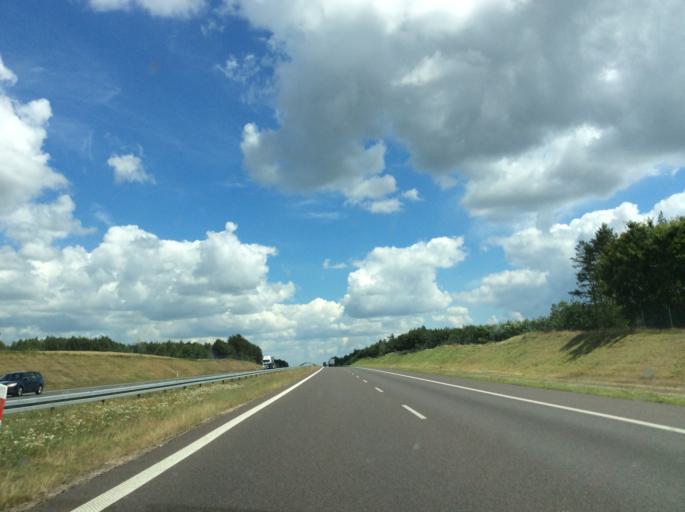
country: PL
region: Greater Poland Voivodeship
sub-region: Powiat kolski
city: Koscielec
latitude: 52.1415
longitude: 18.5458
